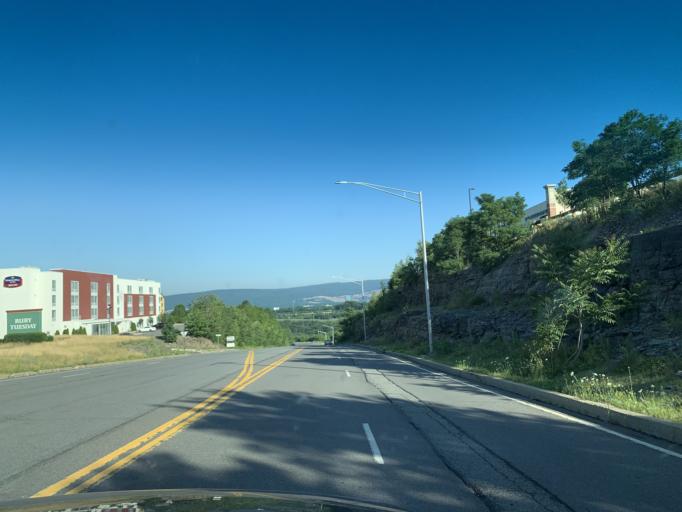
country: US
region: Pennsylvania
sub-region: Lackawanna County
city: Taylor
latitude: 41.3632
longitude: -75.6802
